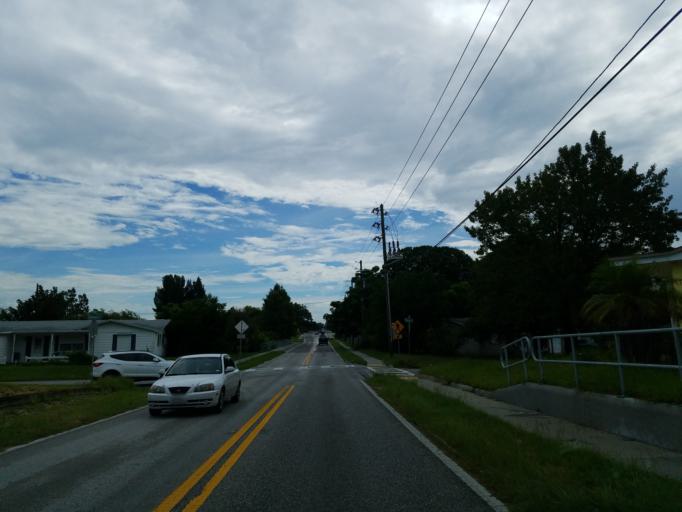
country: US
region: Florida
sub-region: Pasco County
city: Beacon Square
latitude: 28.2096
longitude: -82.7434
